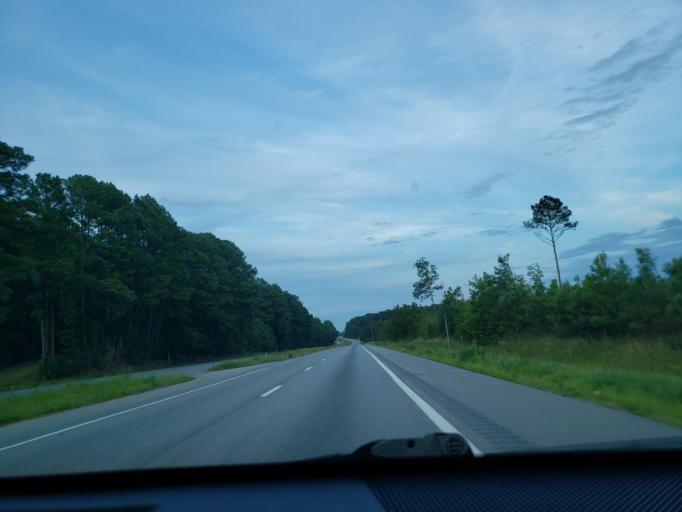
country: US
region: Virginia
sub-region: Sussex County
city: Sussex
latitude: 36.7044
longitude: -77.2800
